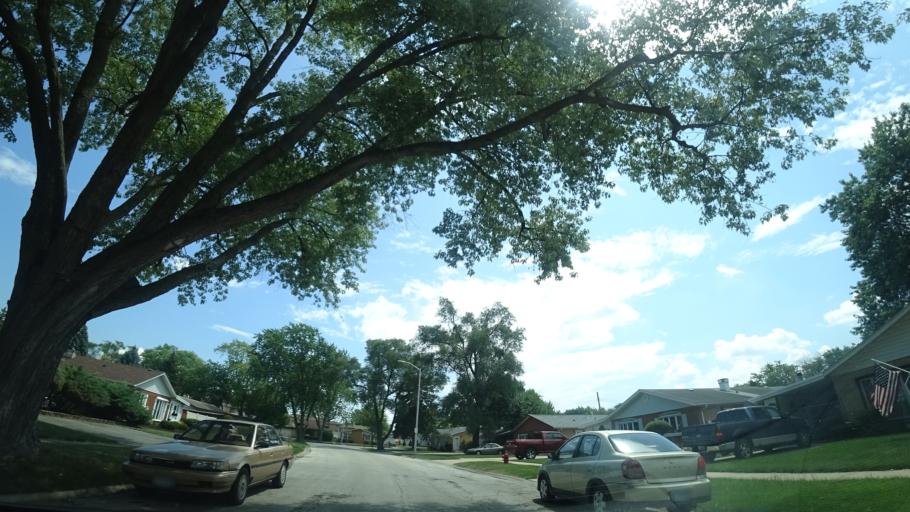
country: US
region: Illinois
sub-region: Cook County
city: Alsip
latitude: 41.6786
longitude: -87.7239
